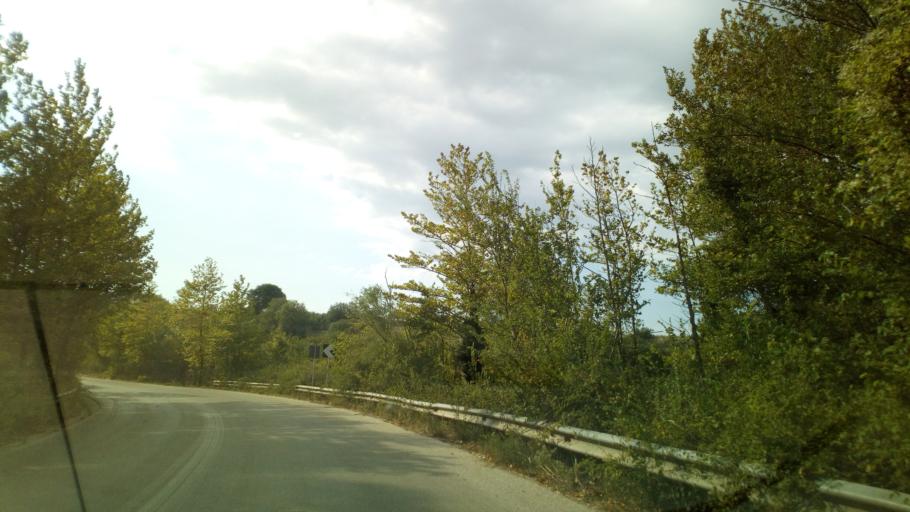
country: GR
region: Central Macedonia
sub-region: Nomos Thessalonikis
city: Gerakarou
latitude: 40.5894
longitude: 23.2533
